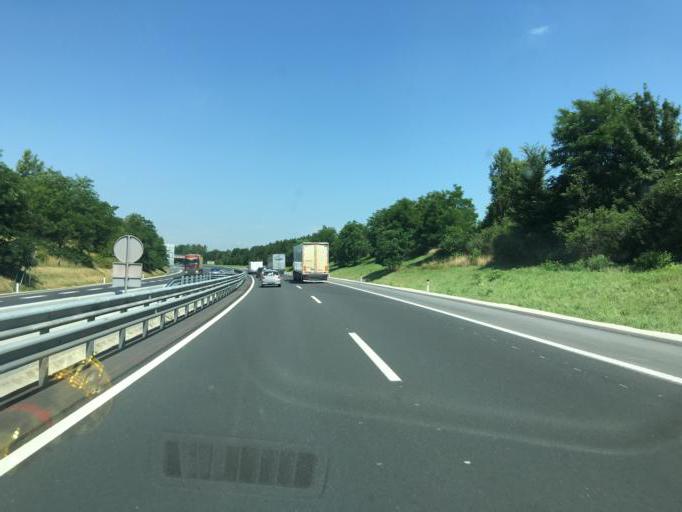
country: SI
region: Hoce-Slivnica
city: Rogoza
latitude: 46.4957
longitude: 15.6701
